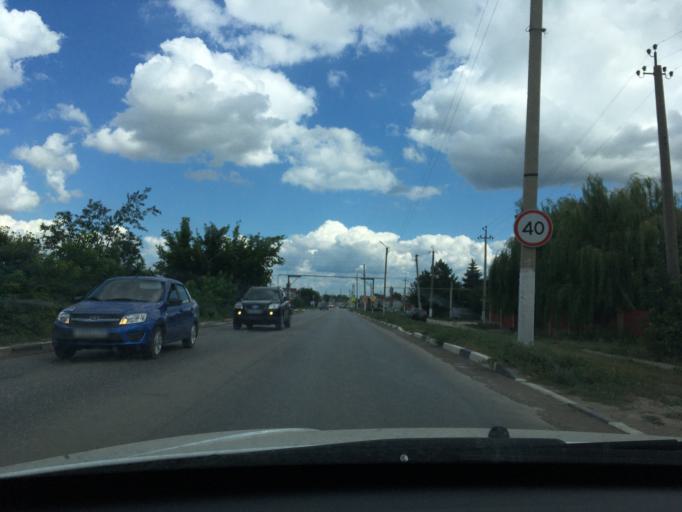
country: RU
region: Samara
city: Bezenchuk
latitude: 52.9893
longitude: 49.4357
